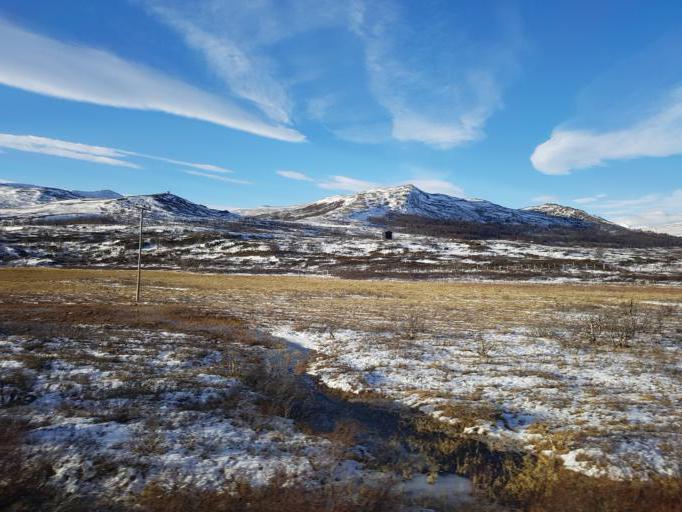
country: NO
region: Oppland
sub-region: Dovre
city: Dovre
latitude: 62.2317
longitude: 9.5402
